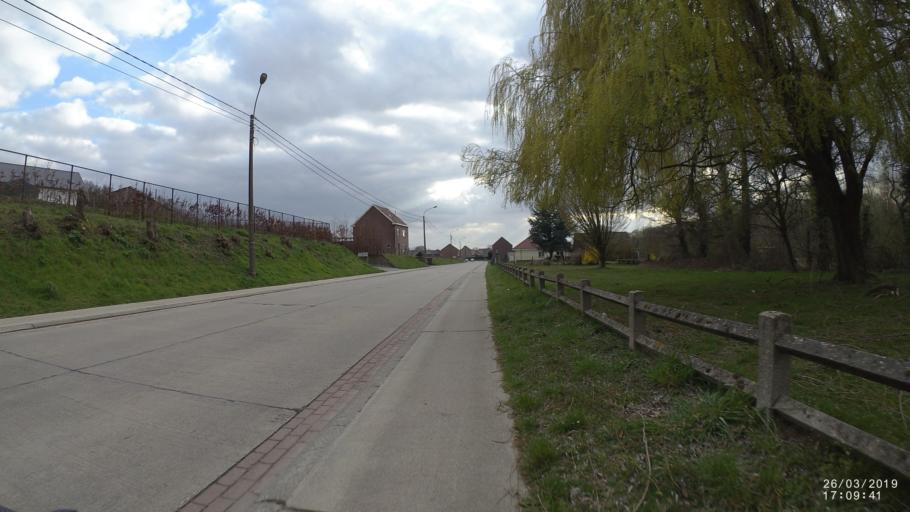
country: BE
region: Flanders
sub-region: Provincie Vlaams-Brabant
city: Huldenberg
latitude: 50.8391
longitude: 4.5768
